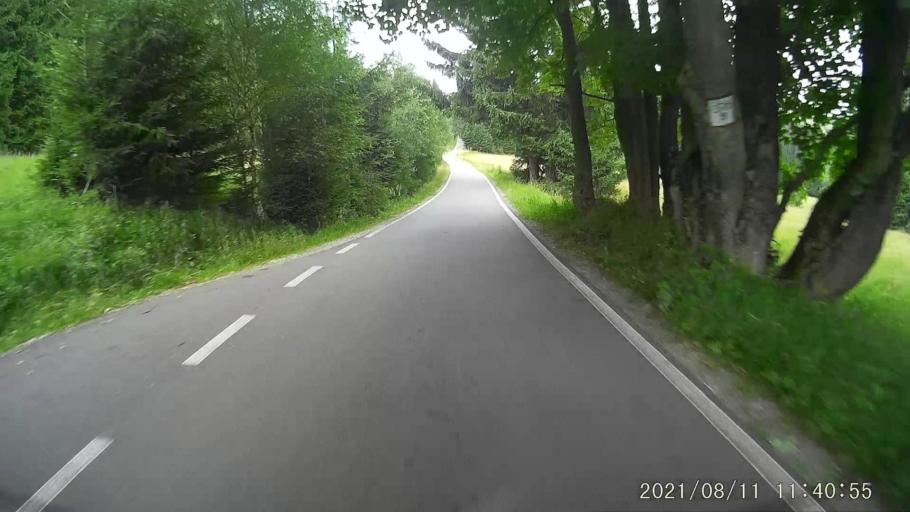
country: PL
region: Lower Silesian Voivodeship
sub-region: Powiat klodzki
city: Stronie Slaskie
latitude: 50.2547
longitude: 16.8336
